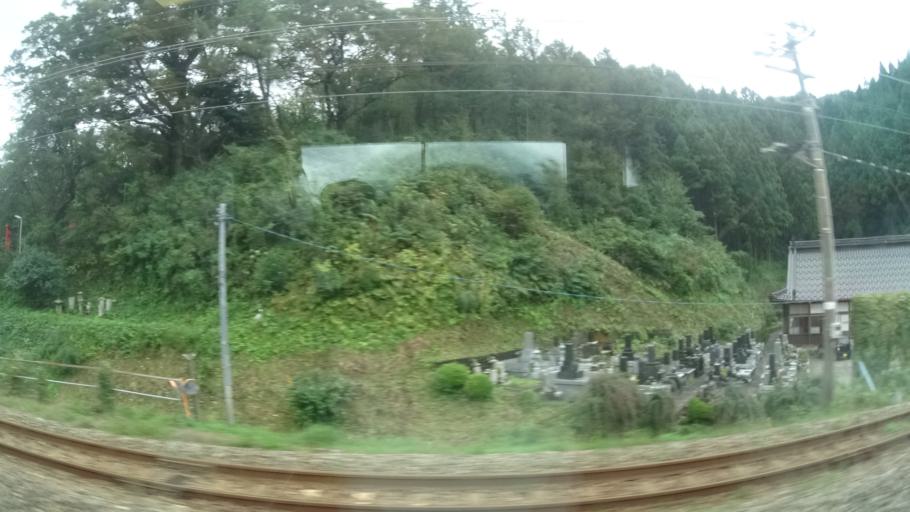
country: JP
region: Yamagata
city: Tsuruoka
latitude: 38.7005
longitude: 139.6682
